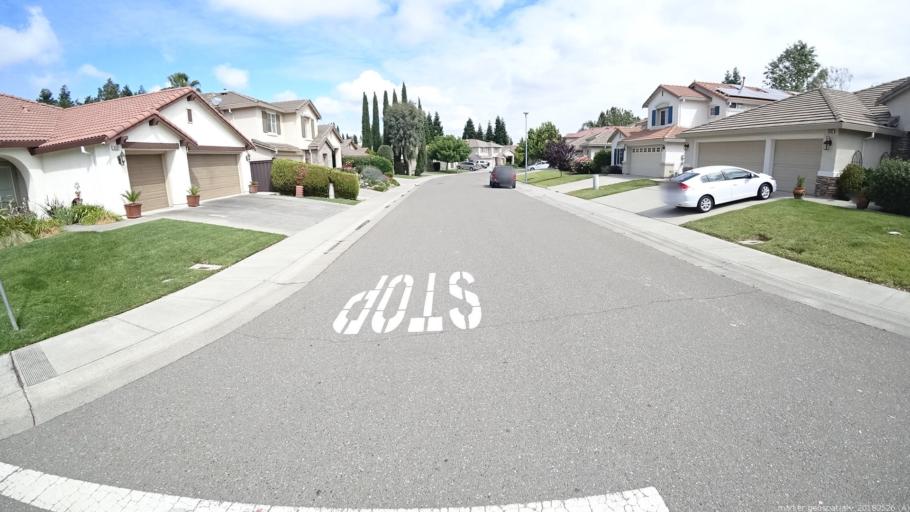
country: US
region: California
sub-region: Yolo County
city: West Sacramento
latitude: 38.6050
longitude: -121.5384
